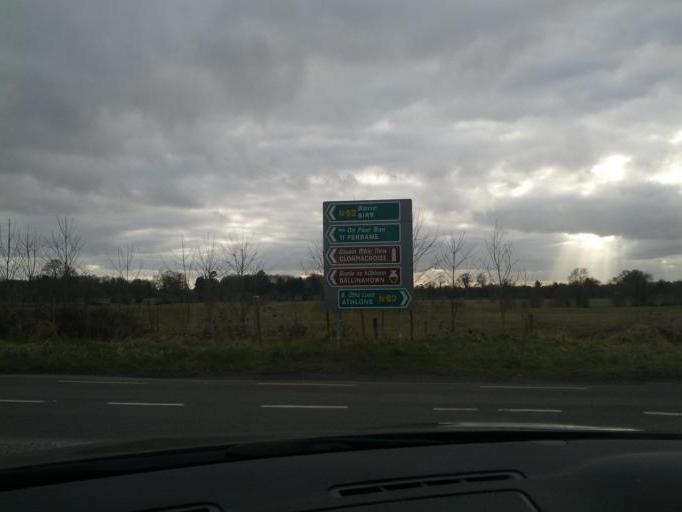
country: IE
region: Leinster
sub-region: Uibh Fhaili
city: Ferbane
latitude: 53.3607
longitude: -7.8497
